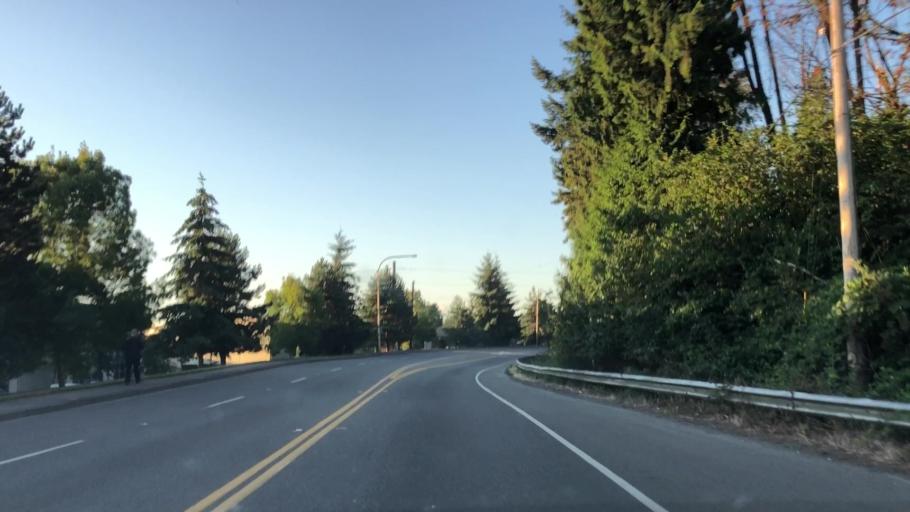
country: US
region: Washington
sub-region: King County
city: Lakeland North
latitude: 47.3382
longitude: -122.2480
